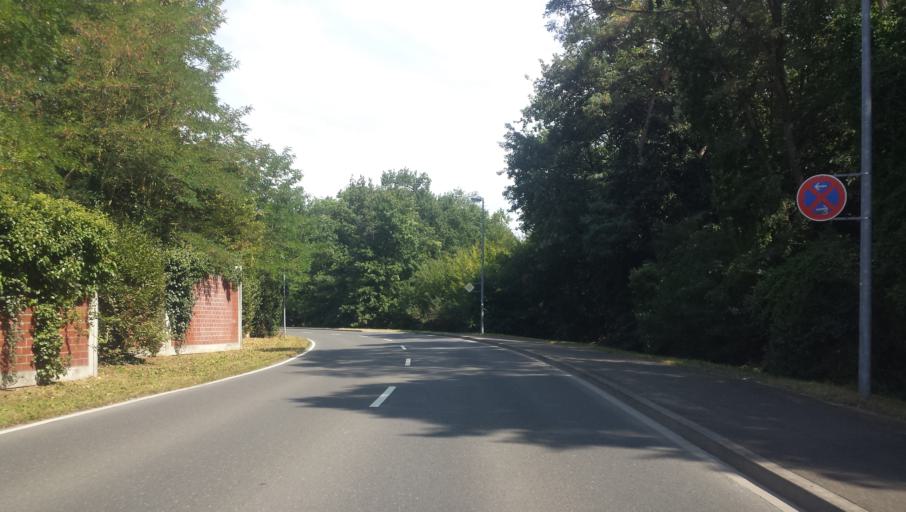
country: DE
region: Baden-Wuerttemberg
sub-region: Karlsruhe Region
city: Hockenheim
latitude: 49.3279
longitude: 8.5593
